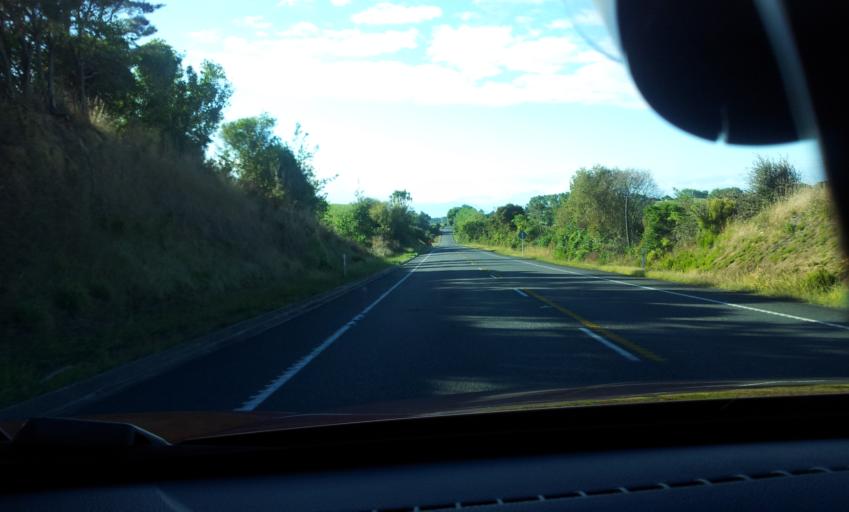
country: NZ
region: Waikato
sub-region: Hauraki District
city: Ngatea
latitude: -37.3146
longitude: 175.3951
